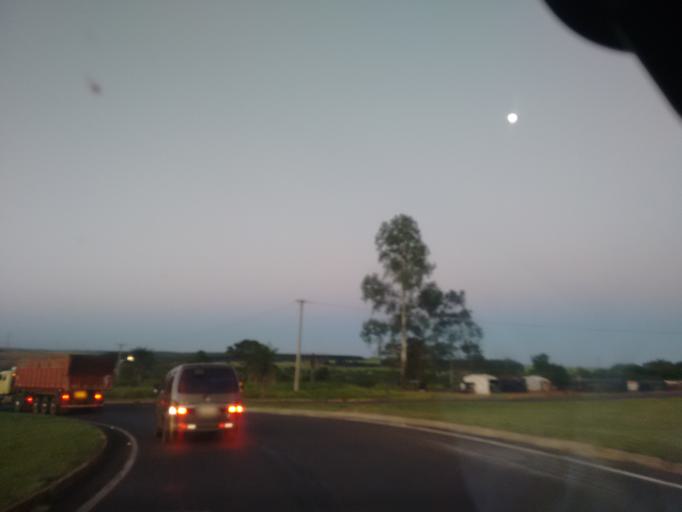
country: BR
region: Mato Grosso do Sul
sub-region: Navirai
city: Navirai
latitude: -23.2474
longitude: -54.2249
